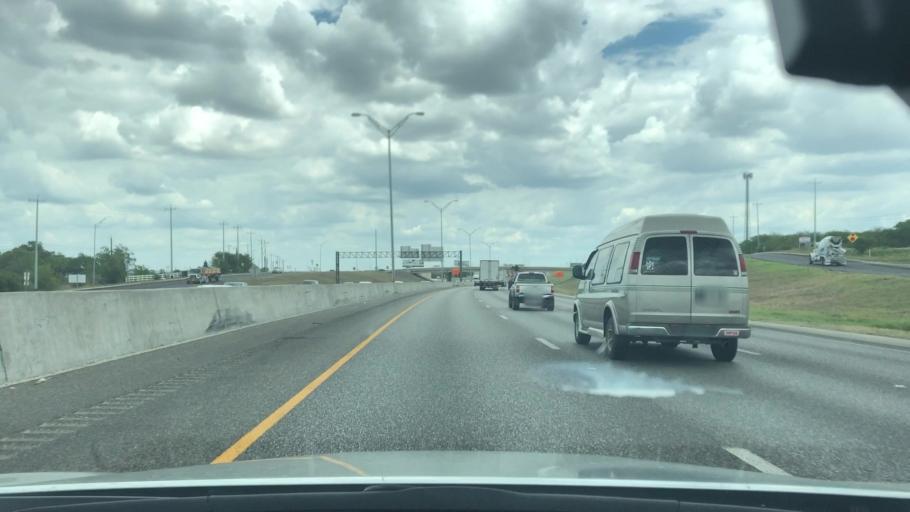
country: US
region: Texas
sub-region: Guadalupe County
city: Northcliff
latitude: 29.6157
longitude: -98.2602
